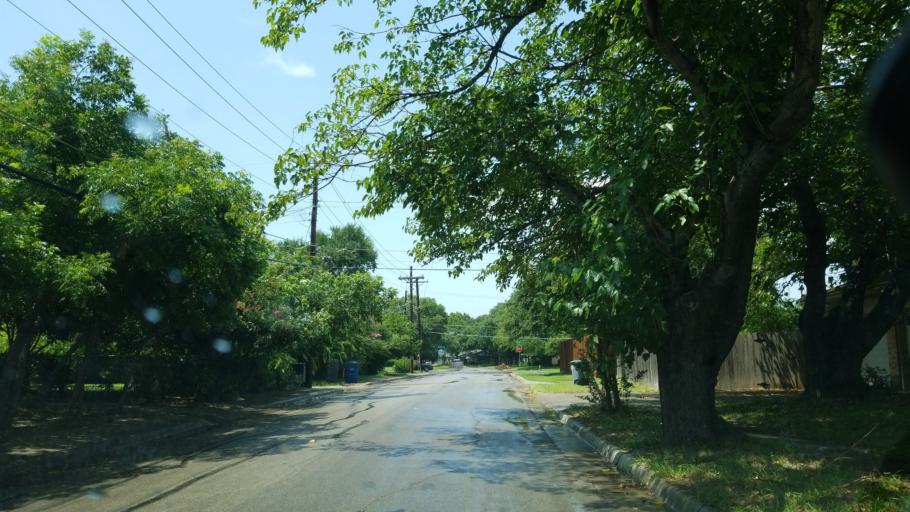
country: US
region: Texas
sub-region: Dallas County
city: Farmers Branch
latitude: 32.8801
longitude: -96.8718
